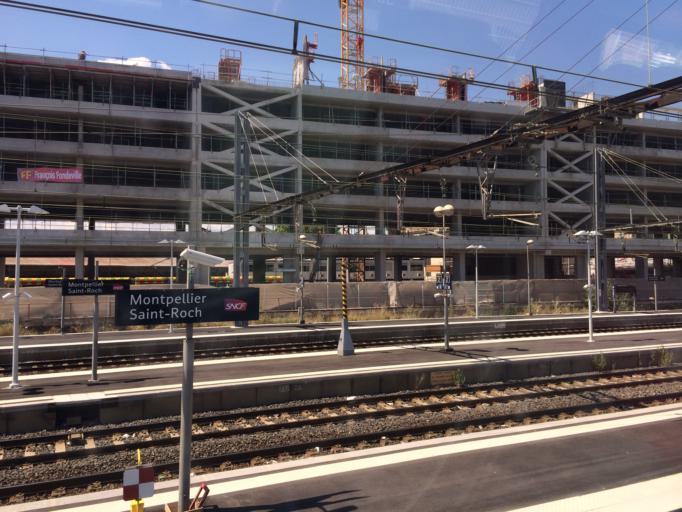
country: FR
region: Languedoc-Roussillon
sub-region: Departement de l'Herault
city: Montpellier
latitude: 43.6025
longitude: 3.8786
